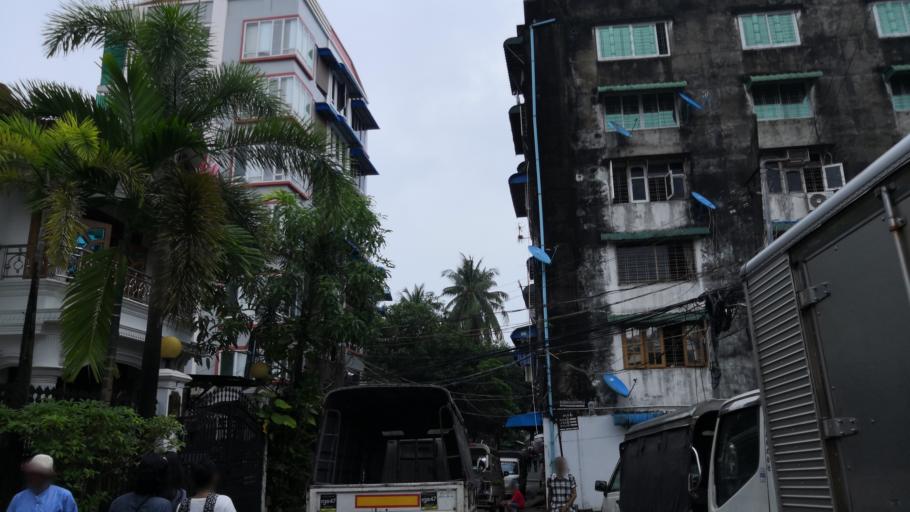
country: MM
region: Yangon
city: Yangon
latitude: 16.7982
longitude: 96.1547
